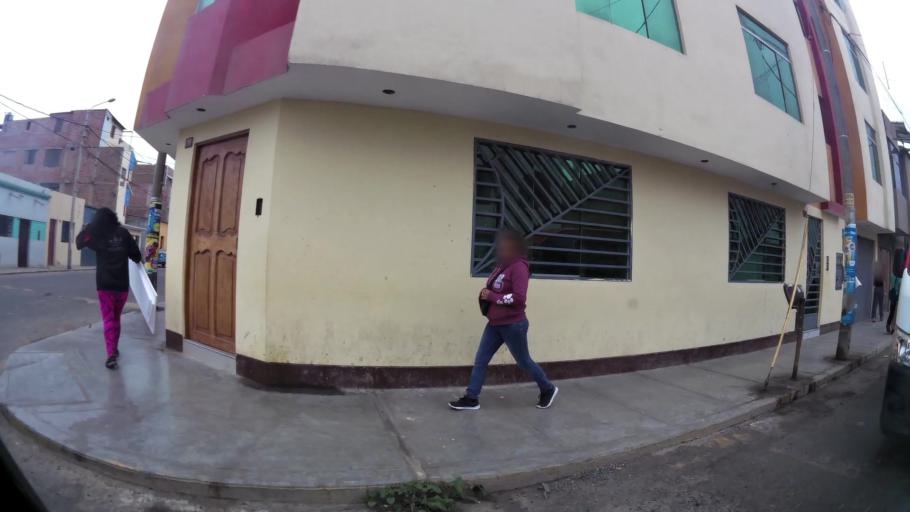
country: PE
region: La Libertad
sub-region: Provincia de Trujillo
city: Trujillo
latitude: -8.1208
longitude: -79.0231
